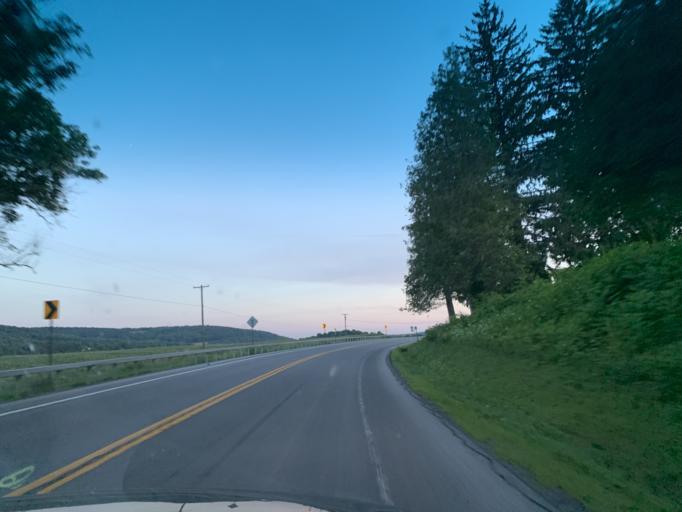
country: US
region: New York
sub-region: Chenango County
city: New Berlin
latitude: 42.7609
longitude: -75.2827
